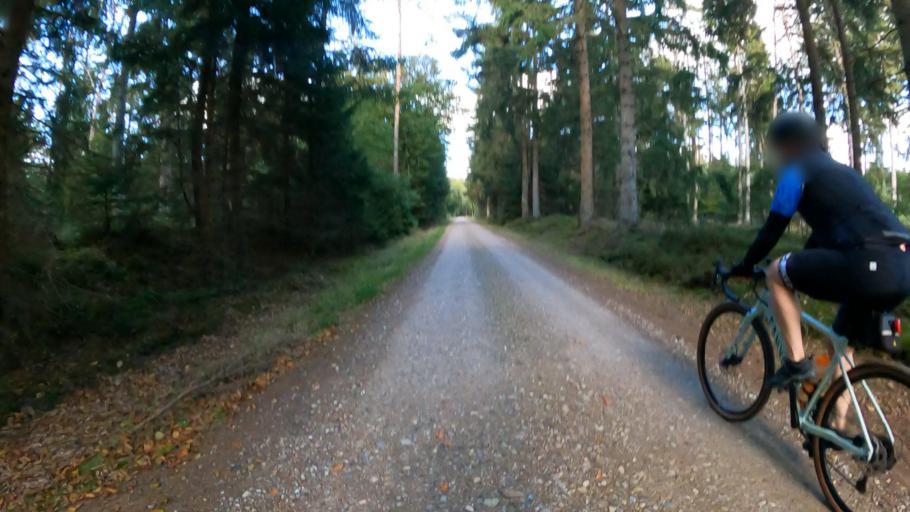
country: DE
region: Schleswig-Holstein
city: Heidmuhlen
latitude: 53.9431
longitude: 10.0998
